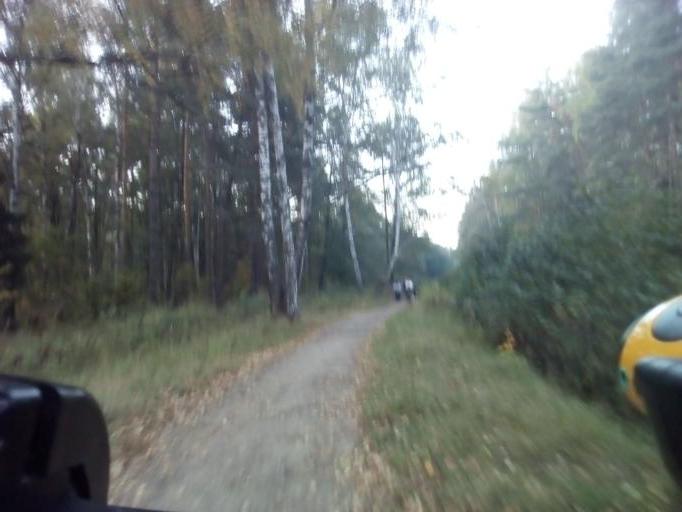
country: RU
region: Moskovskaya
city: Ramenskoye
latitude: 55.5954
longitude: 38.2141
